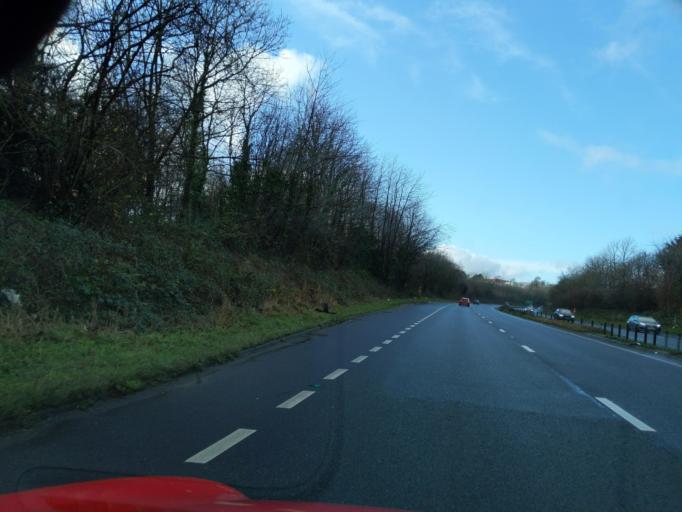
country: GB
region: England
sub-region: Plymouth
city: Plymouth
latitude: 50.4028
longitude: -4.1479
